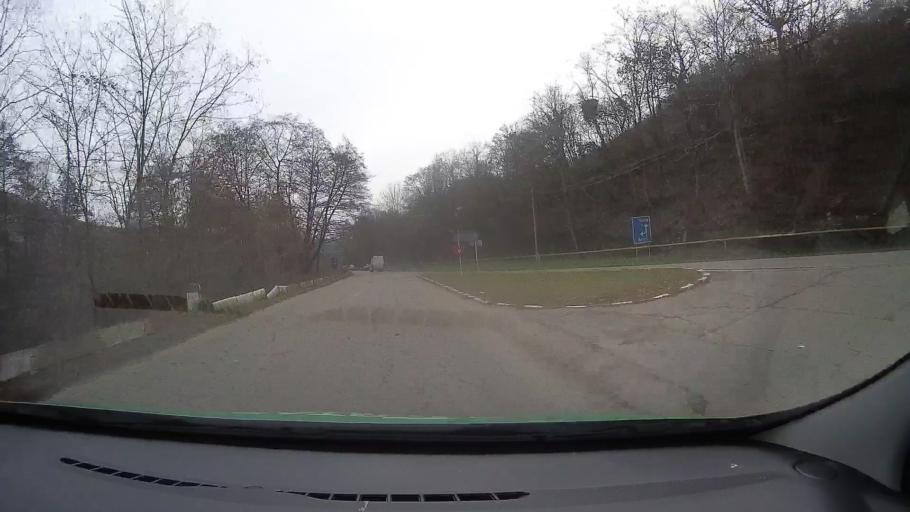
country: RO
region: Hunedoara
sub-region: Comuna Geoagiu
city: Geoagiu
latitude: 45.9393
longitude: 23.1829
